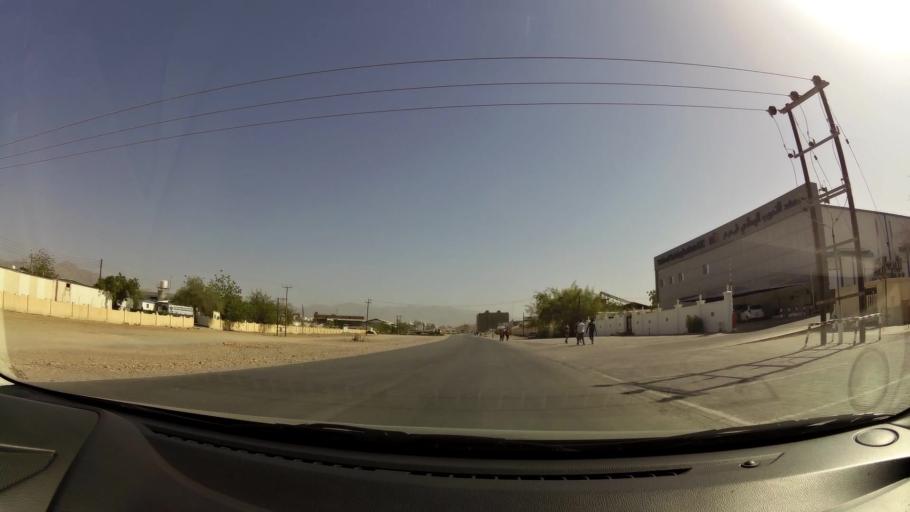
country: OM
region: Muhafazat Masqat
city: Bawshar
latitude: 23.5710
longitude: 58.3503
